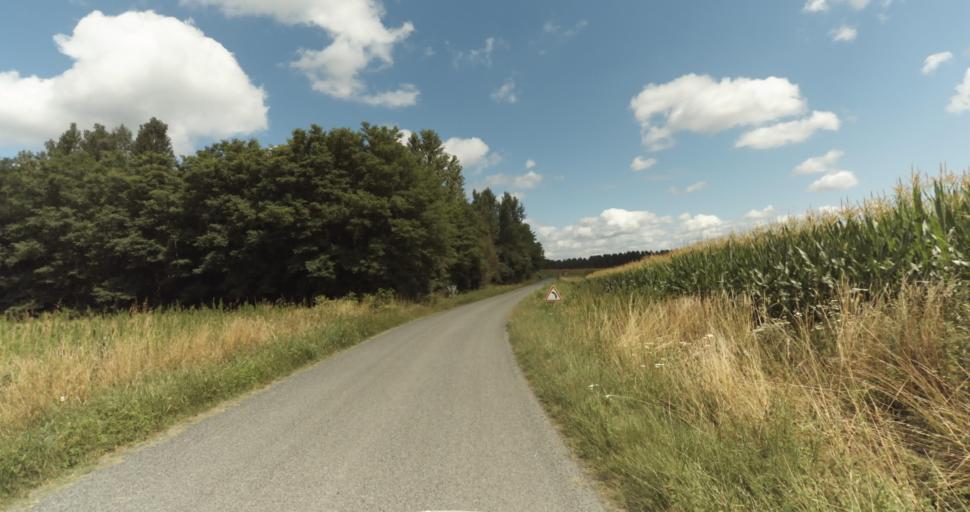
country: FR
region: Aquitaine
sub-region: Departement de la Gironde
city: Bazas
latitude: 44.4747
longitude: -0.1625
